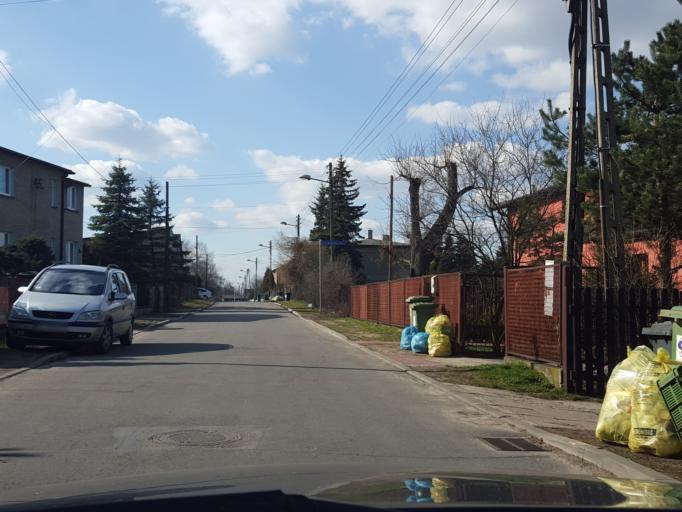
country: PL
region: Silesian Voivodeship
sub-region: Ruda Slaska
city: Ruda Slaska
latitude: 50.2316
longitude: 18.8671
